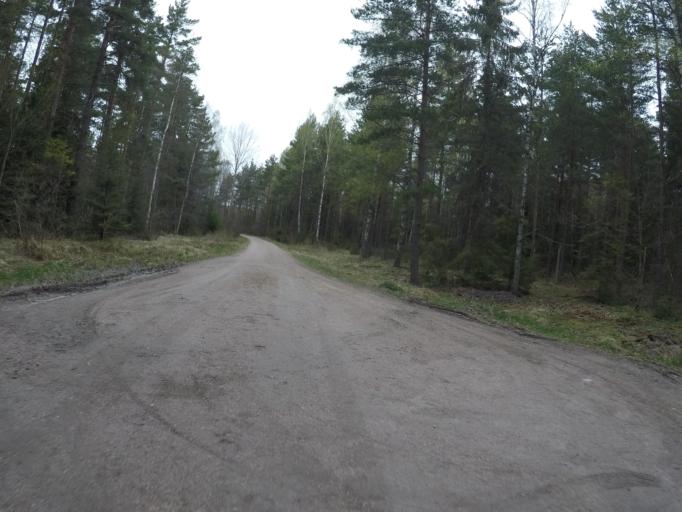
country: SE
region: Soedermanland
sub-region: Eskilstuna Kommun
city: Kvicksund
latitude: 59.3953
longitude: 16.2593
